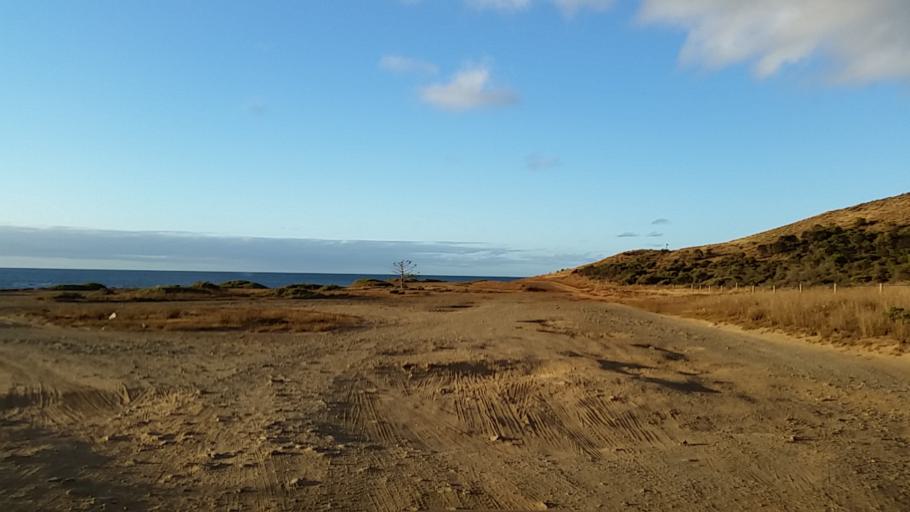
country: AU
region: South Australia
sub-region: Yankalilla
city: Normanville
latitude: -35.6031
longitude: 138.0954
